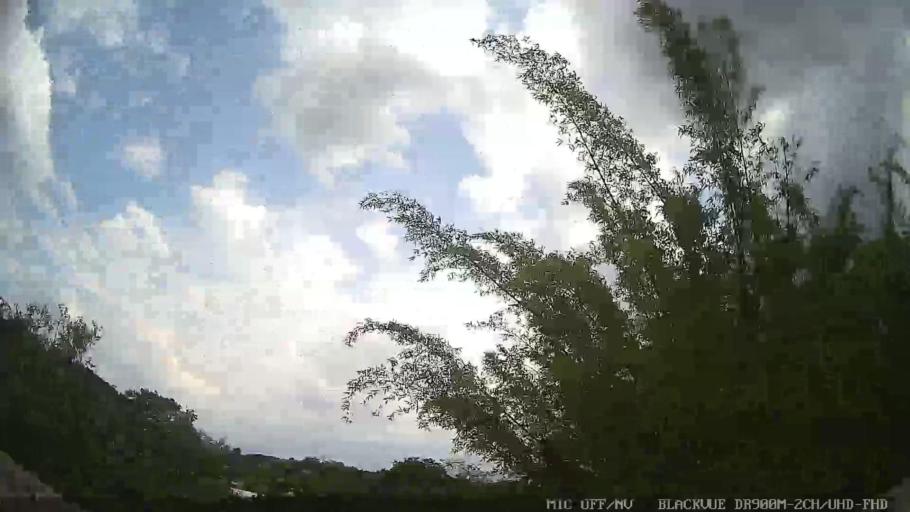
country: BR
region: Sao Paulo
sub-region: Louveira
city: Louveira
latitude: -23.0873
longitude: -46.9298
